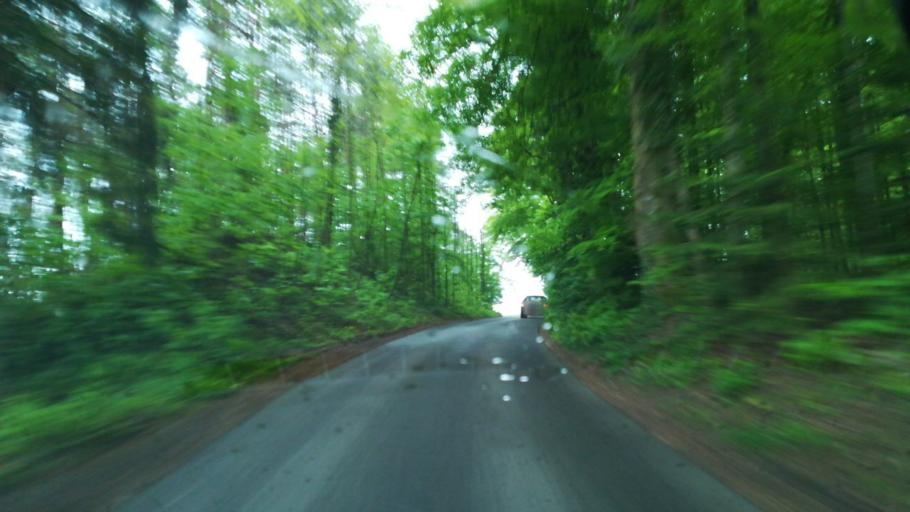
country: CH
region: Zurich
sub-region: Bezirk Buelach
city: Hochfelden
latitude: 47.5197
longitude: 8.4973
